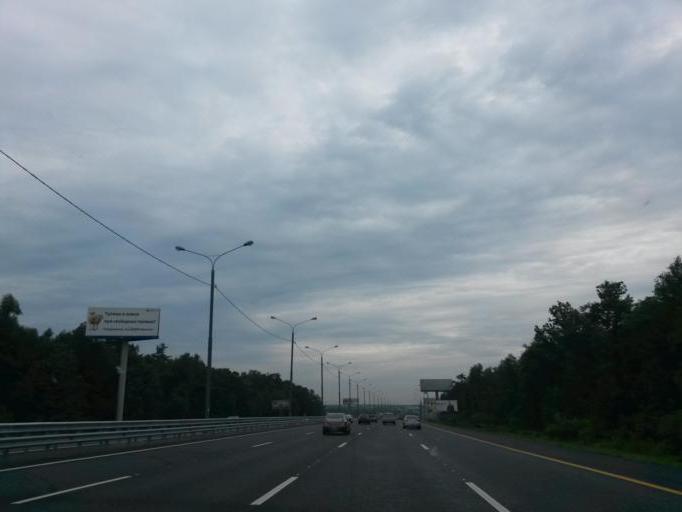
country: RU
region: Moskovskaya
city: Shcherbinka
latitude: 55.5166
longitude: 37.6086
